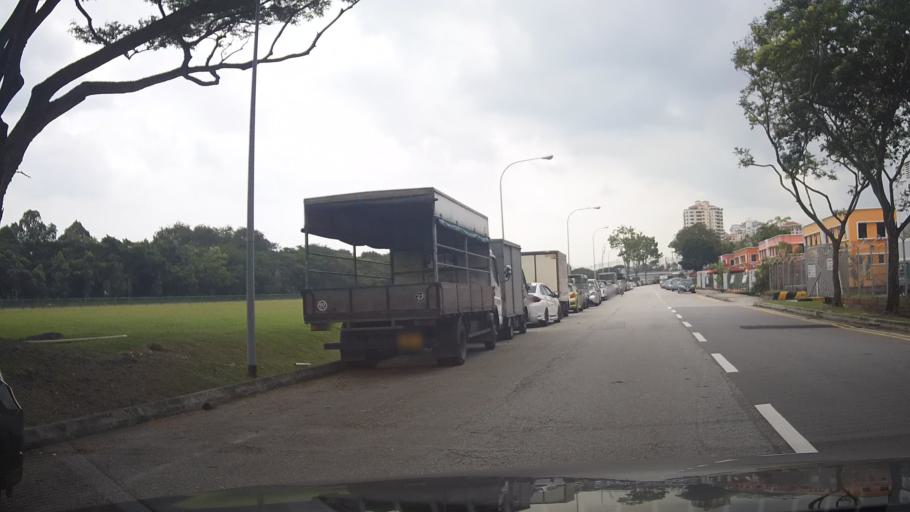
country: SG
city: Singapore
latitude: 1.3032
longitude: 103.8809
